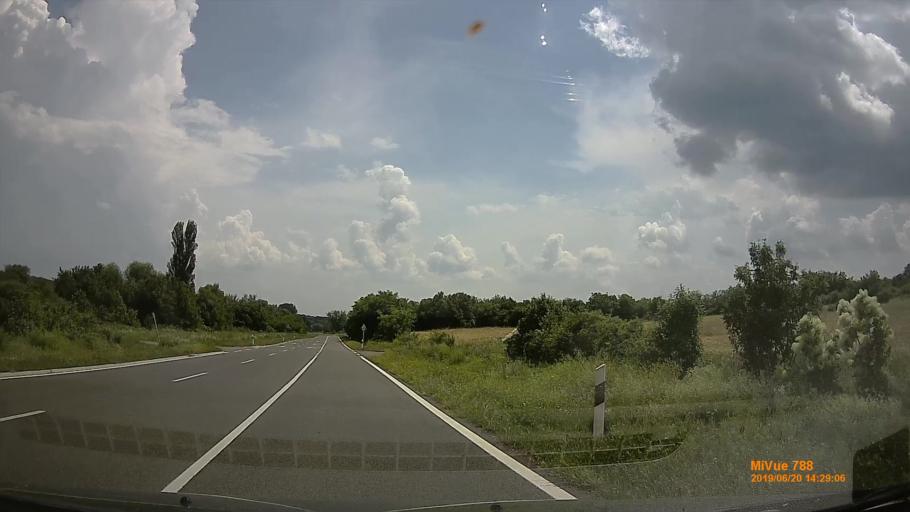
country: HU
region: Baranya
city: Hosszuheteny
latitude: 46.1641
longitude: 18.3419
